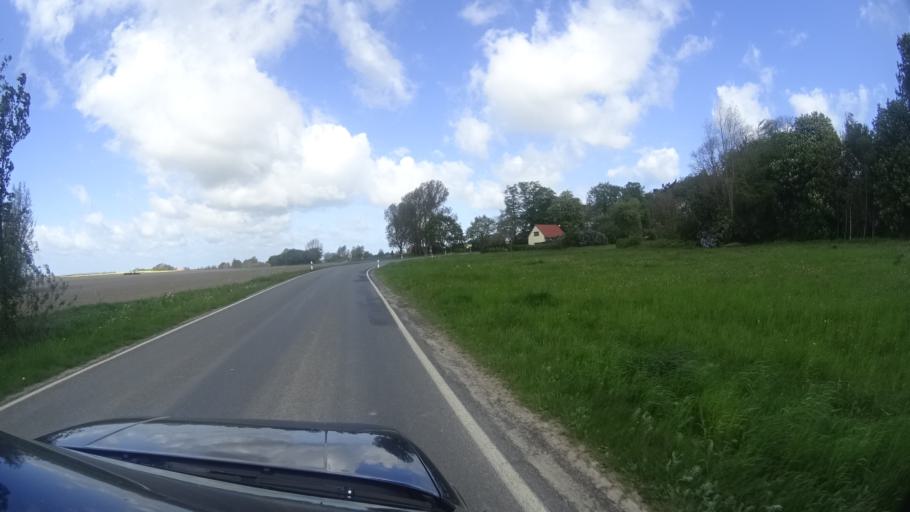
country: DE
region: Mecklenburg-Vorpommern
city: Saal
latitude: 54.3192
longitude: 12.5790
